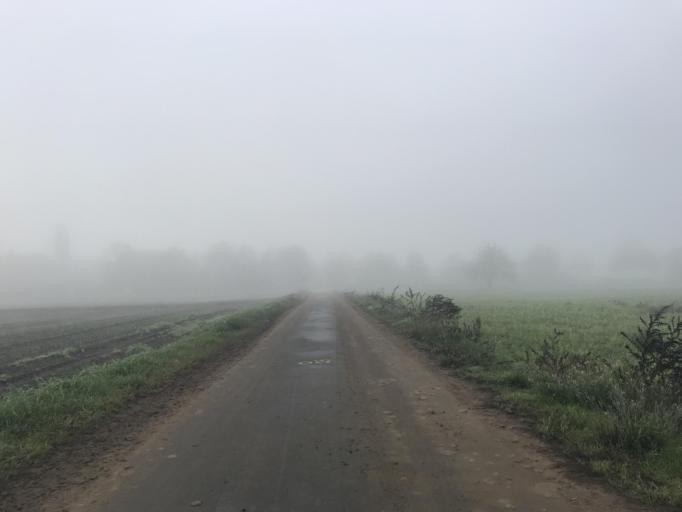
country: DE
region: Rheinland-Pfalz
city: Mainz
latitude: 50.0225
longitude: 8.2864
